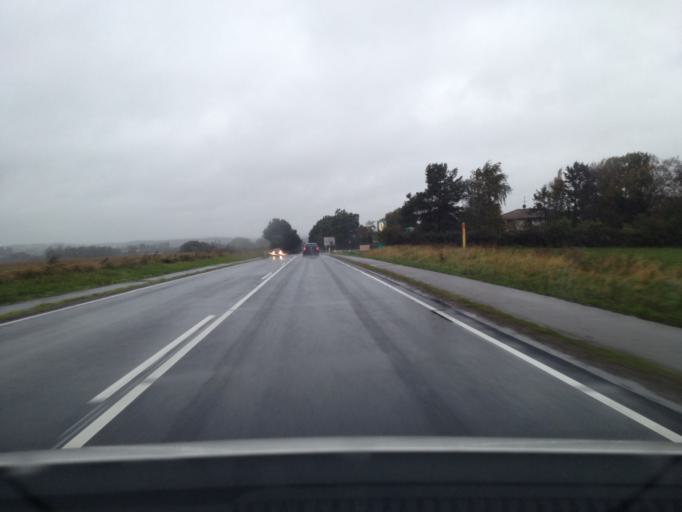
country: DK
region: Zealand
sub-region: Holbaek Kommune
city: Tollose
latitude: 55.5396
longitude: 11.7111
